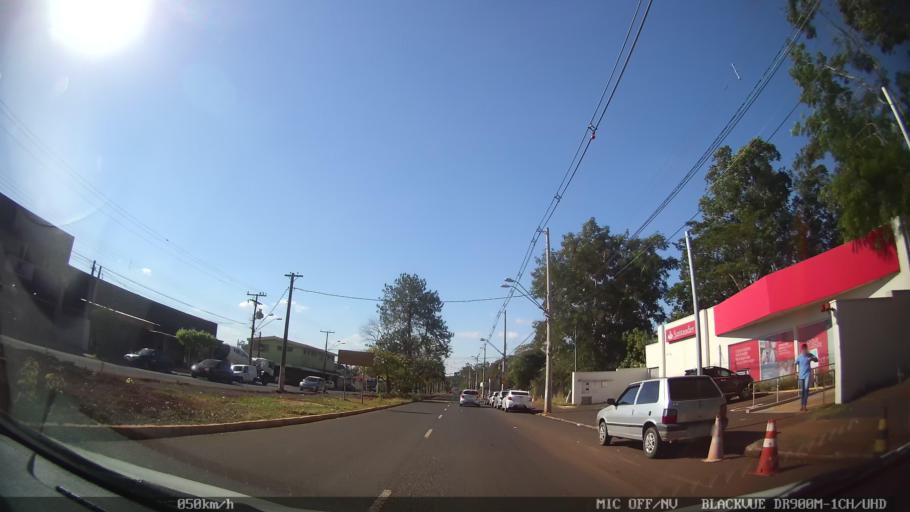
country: BR
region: Sao Paulo
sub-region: Ribeirao Preto
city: Ribeirao Preto
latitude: -21.1570
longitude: -47.7844
